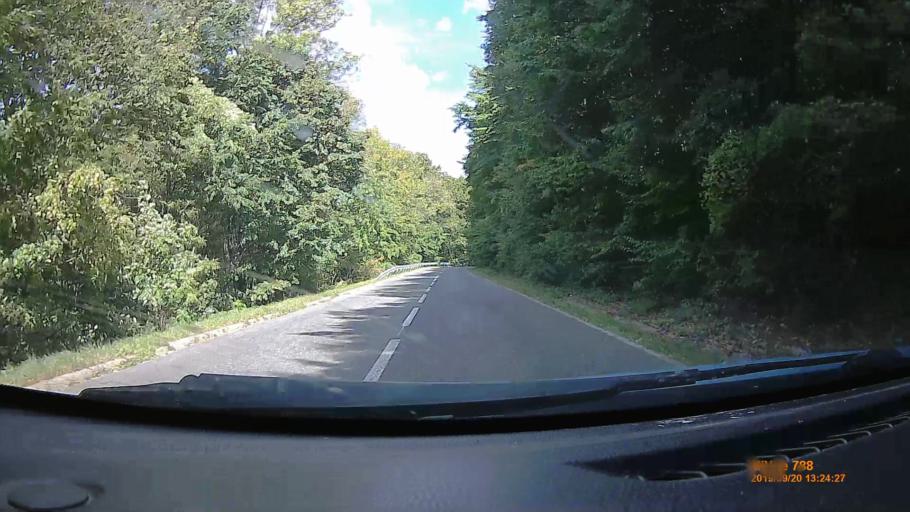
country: HU
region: Heves
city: Felsotarkany
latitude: 48.0382
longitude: 20.4821
